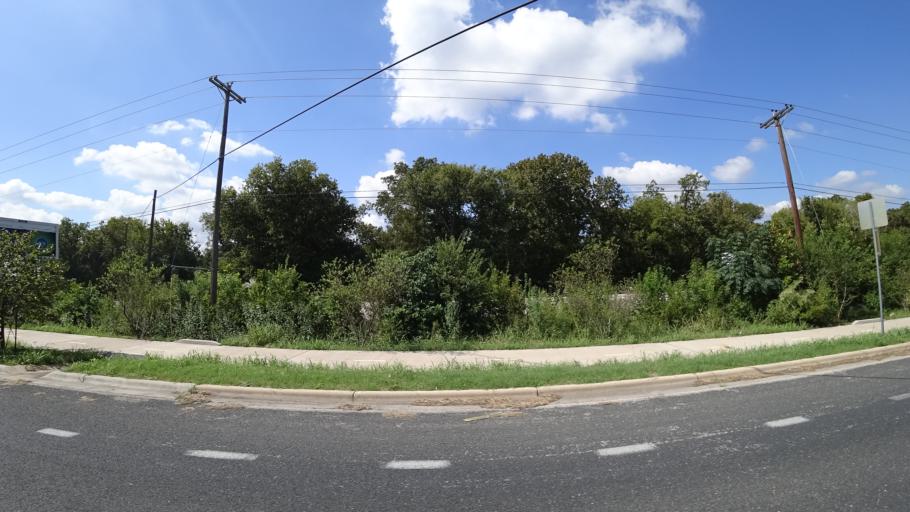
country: US
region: Texas
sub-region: Travis County
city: Austin
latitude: 30.3312
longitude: -97.7157
